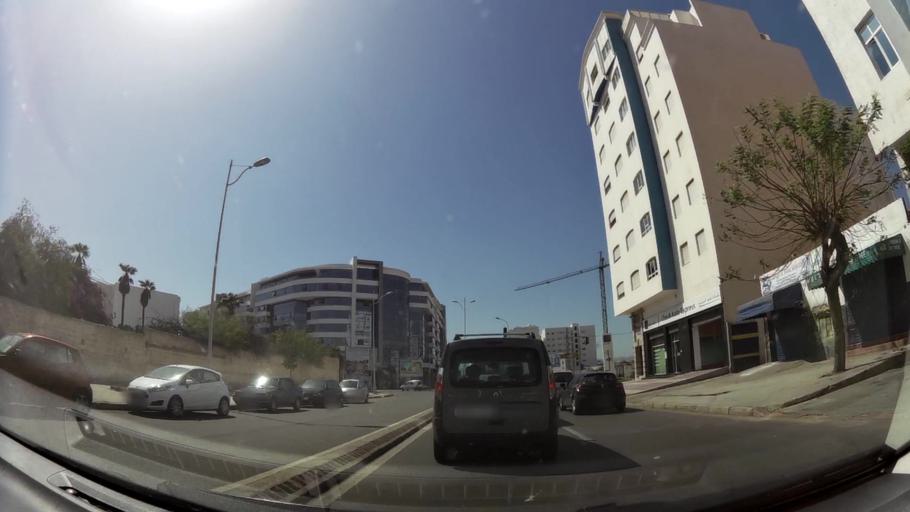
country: MA
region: Oued ed Dahab-Lagouira
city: Dakhla
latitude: 30.4177
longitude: -9.5754
